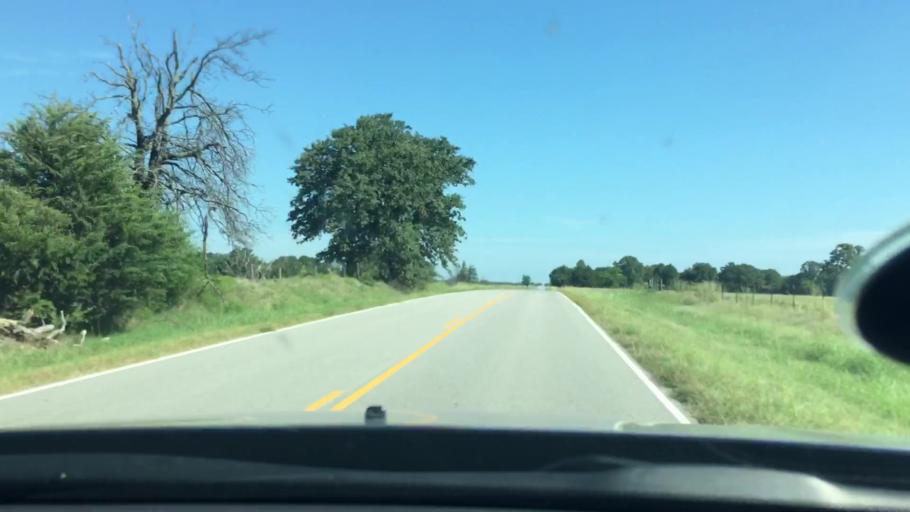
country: US
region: Oklahoma
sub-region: Johnston County
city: Tishomingo
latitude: 34.2980
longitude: -96.5488
